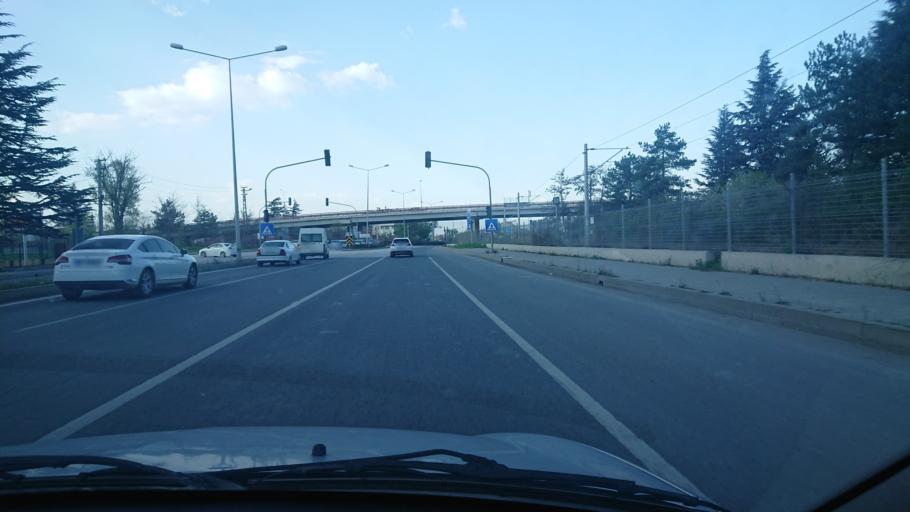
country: TR
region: Eskisehir
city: Eskisehir
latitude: 39.7674
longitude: 30.4802
